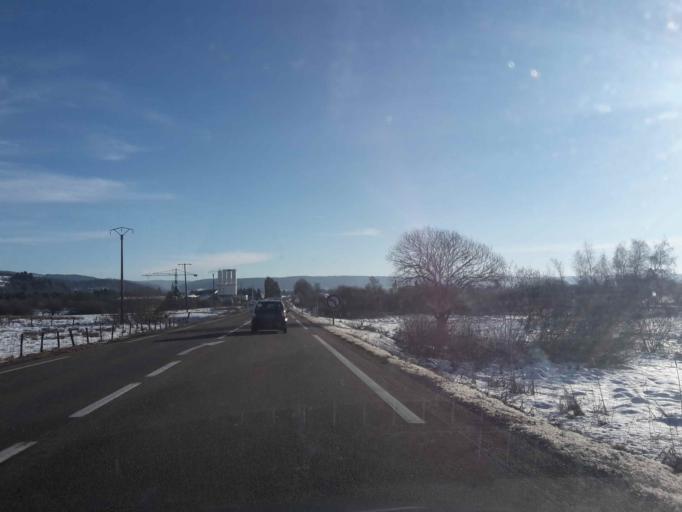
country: FR
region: Franche-Comte
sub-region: Departement du Doubs
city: Doubs
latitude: 46.9472
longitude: 6.3426
